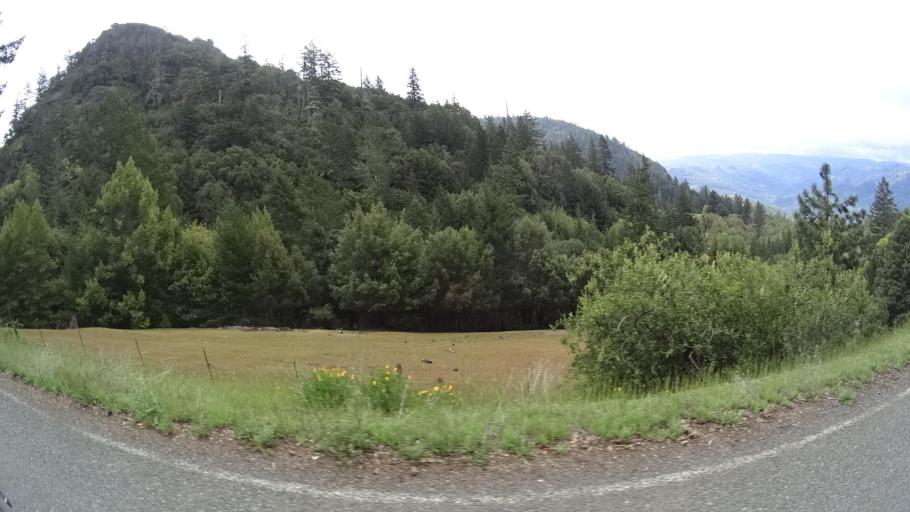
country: US
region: California
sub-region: Humboldt County
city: Redway
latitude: 40.1550
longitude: -123.5547
